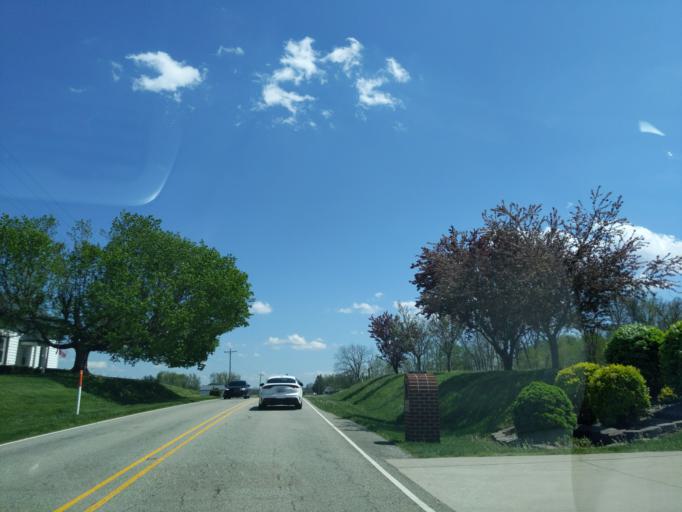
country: US
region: Indiana
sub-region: Decatur County
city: Saint Paul
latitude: 39.4041
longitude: -85.5629
